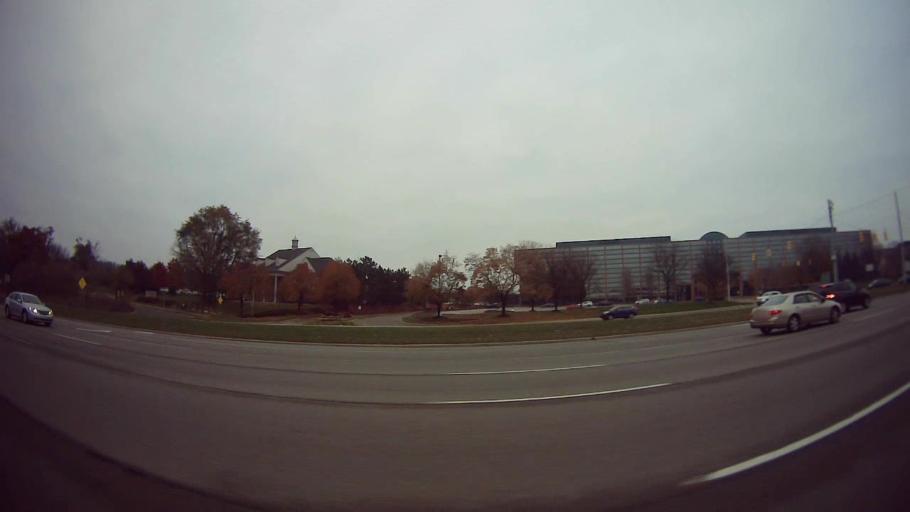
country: US
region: Michigan
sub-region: Oakland County
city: Bingham Farms
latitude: 42.4743
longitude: -83.2840
